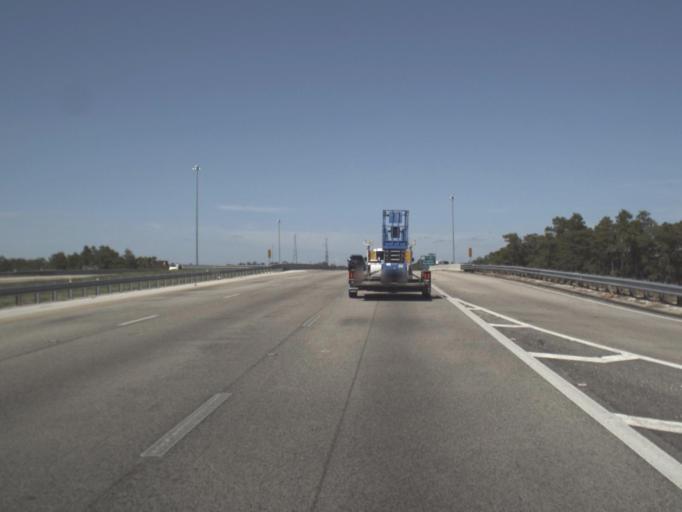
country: US
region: Florida
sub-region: Lee County
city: Fort Myers
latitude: 26.6115
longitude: -81.8027
